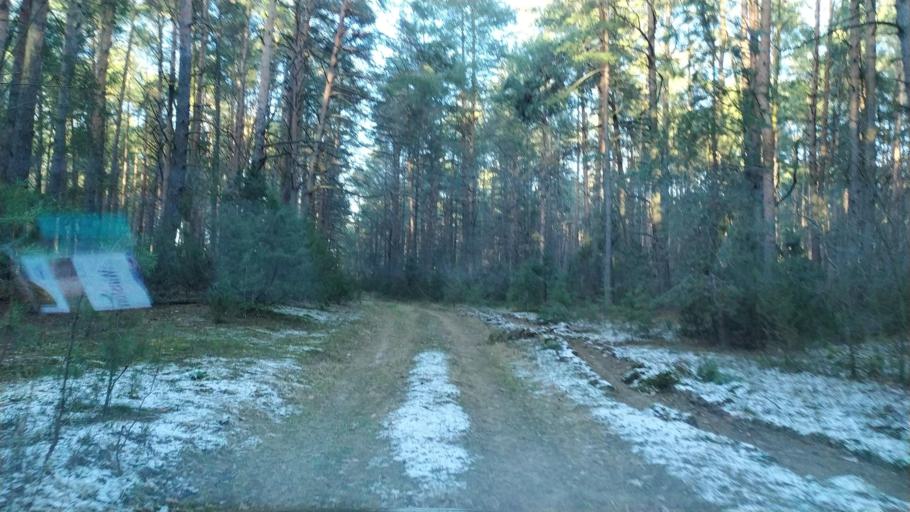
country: BY
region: Brest
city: Pruzhany
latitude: 52.5479
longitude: 24.2733
